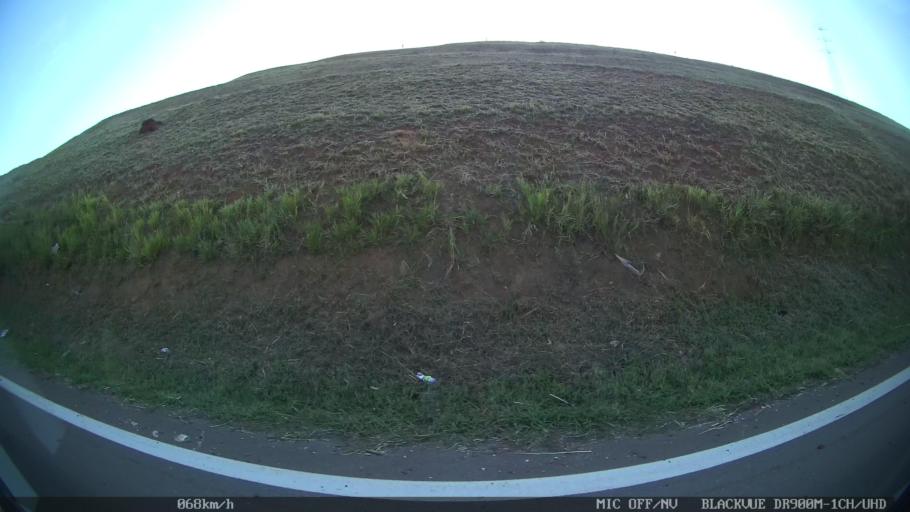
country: BR
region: Sao Paulo
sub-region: Piracicaba
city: Piracicaba
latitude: -22.6889
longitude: -47.5989
